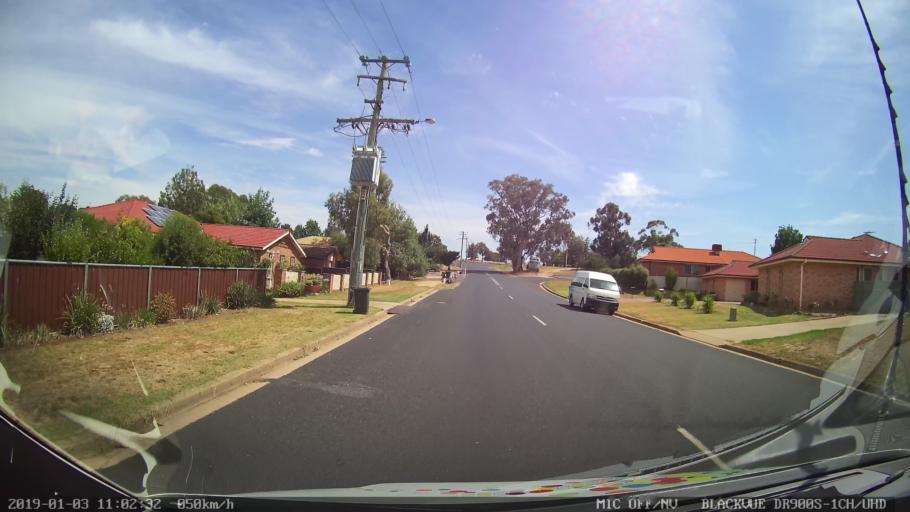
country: AU
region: New South Wales
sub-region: Young
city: Young
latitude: -34.2972
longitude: 148.2984
